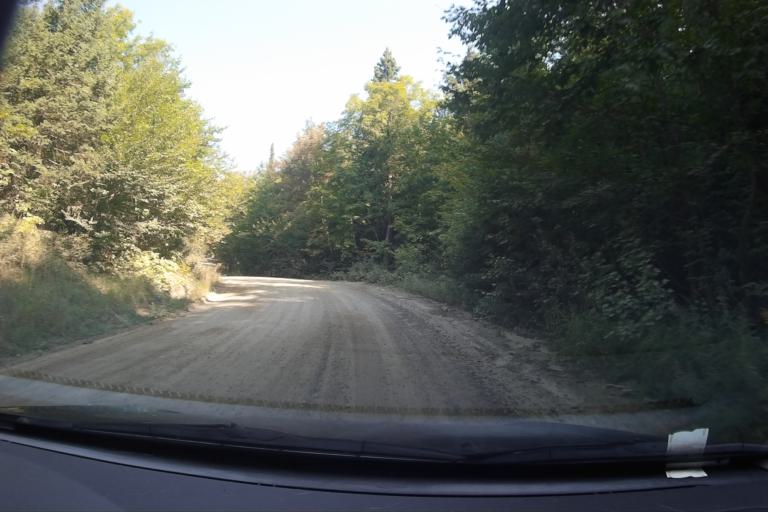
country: CA
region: Ontario
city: Huntsville
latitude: 45.5479
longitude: -78.6955
